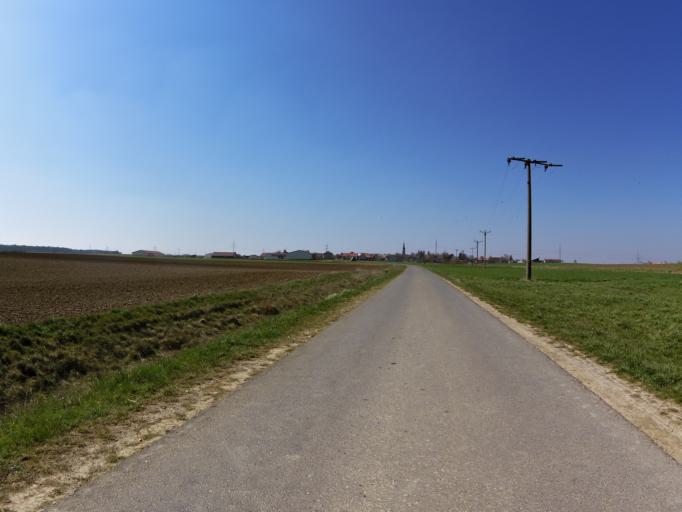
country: DE
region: Bavaria
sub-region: Regierungsbezirk Unterfranken
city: Biebelried
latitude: 49.7448
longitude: 10.0773
